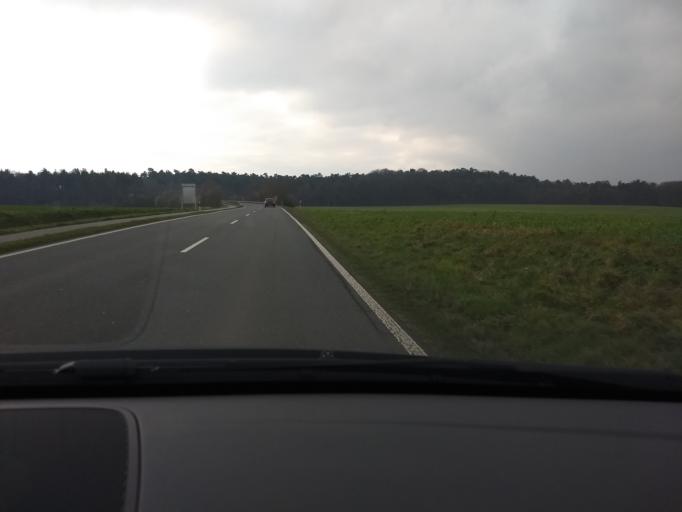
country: DE
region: North Rhine-Westphalia
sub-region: Regierungsbezirk Munster
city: Heiden
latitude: 51.8668
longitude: 6.9190
